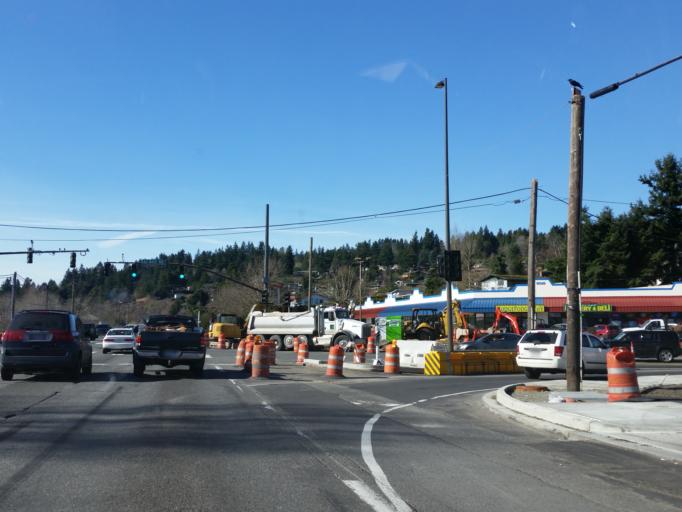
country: US
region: Washington
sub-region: King County
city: Kenmore
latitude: 47.7585
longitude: -122.2617
